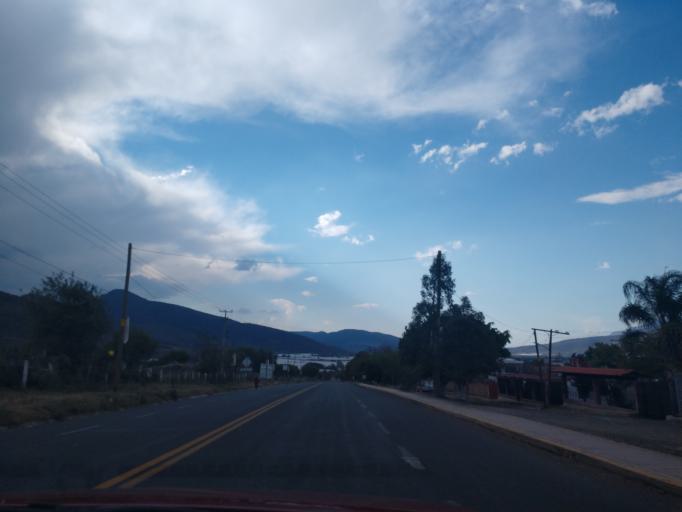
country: MX
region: Jalisco
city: Jocotepec
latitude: 20.2280
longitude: -103.4169
